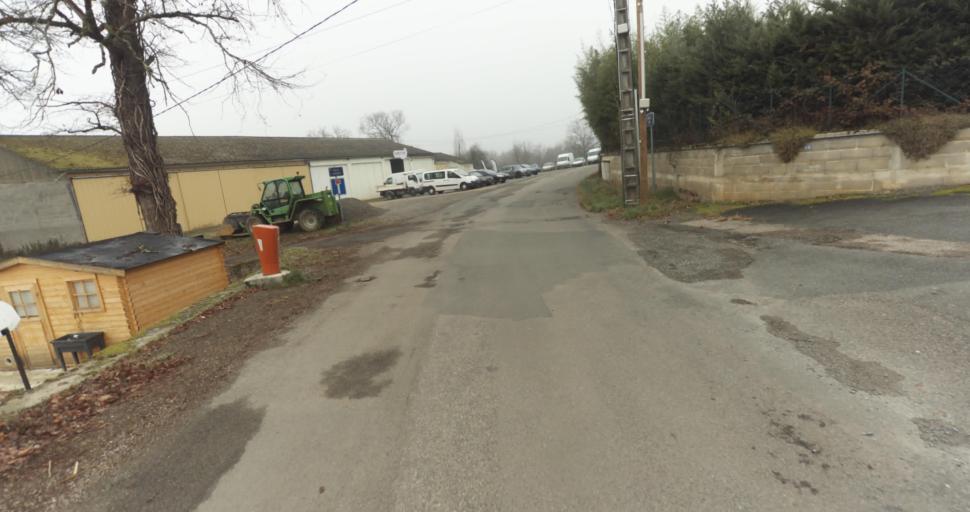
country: FR
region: Midi-Pyrenees
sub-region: Departement du Lot
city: Figeac
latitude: 44.6198
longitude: 2.0367
